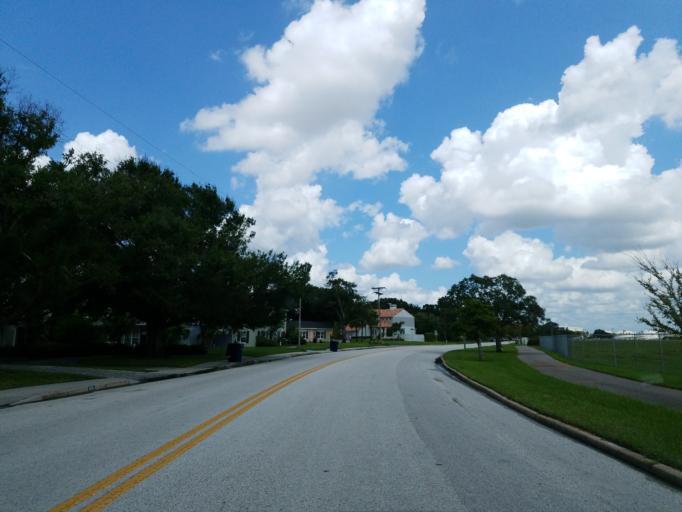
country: US
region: Florida
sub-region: Hillsborough County
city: Tampa
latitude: 27.9148
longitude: -82.4535
